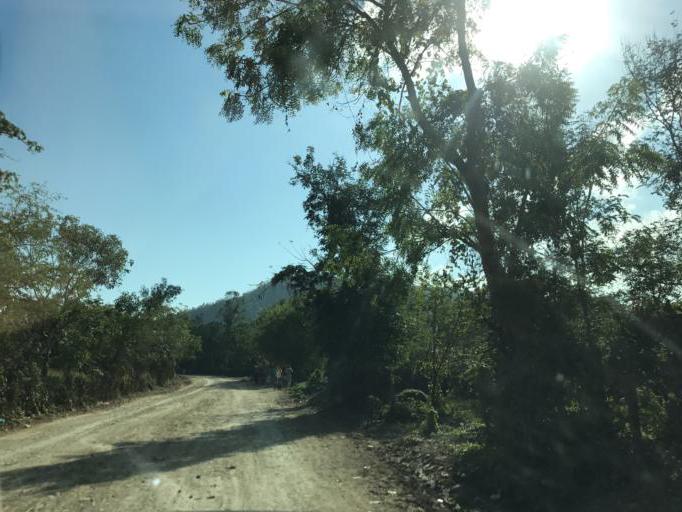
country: HT
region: Sud
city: Fond des Blancs
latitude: 18.2789
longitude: -73.1221
